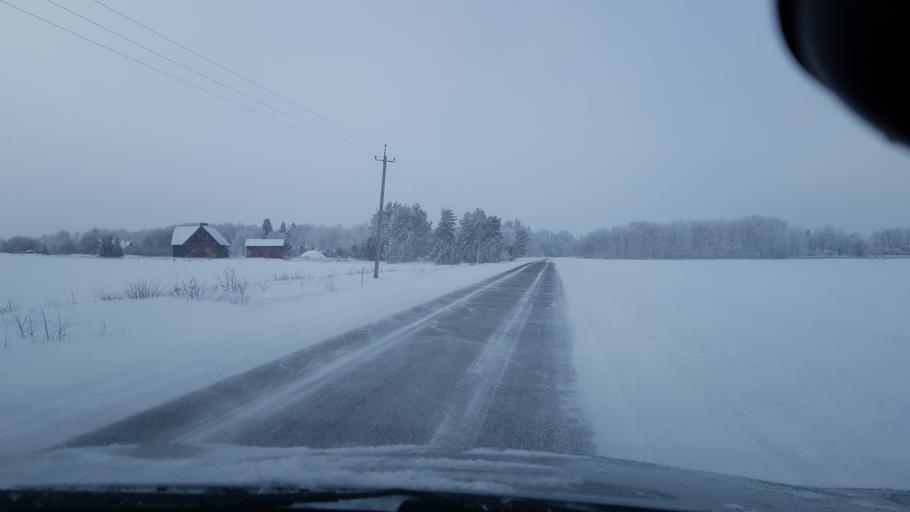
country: EE
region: Harju
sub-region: Keila linn
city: Keila
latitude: 59.3415
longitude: 24.4428
